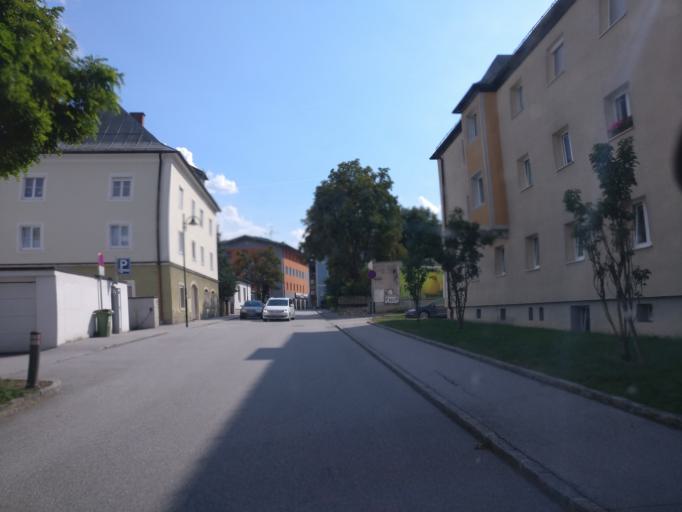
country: AT
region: Salzburg
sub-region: Politischer Bezirk Sankt Johann im Pongau
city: Bischofshofen
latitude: 47.4172
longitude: 13.2178
